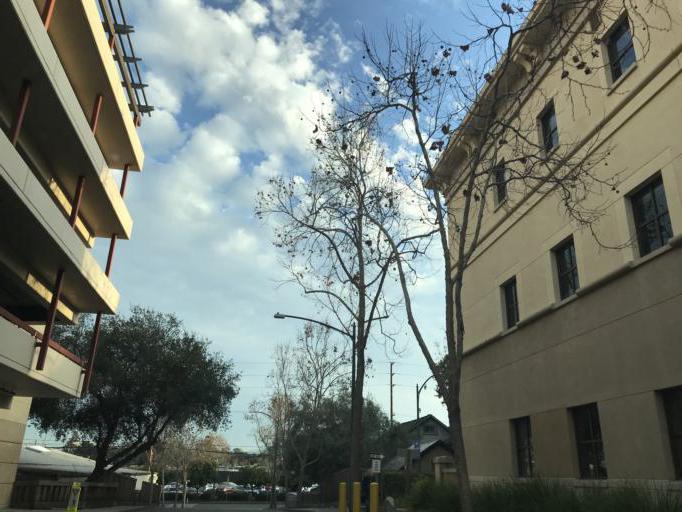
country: US
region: California
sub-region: Santa Clara County
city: Stanford
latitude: 37.4399
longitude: -122.1607
